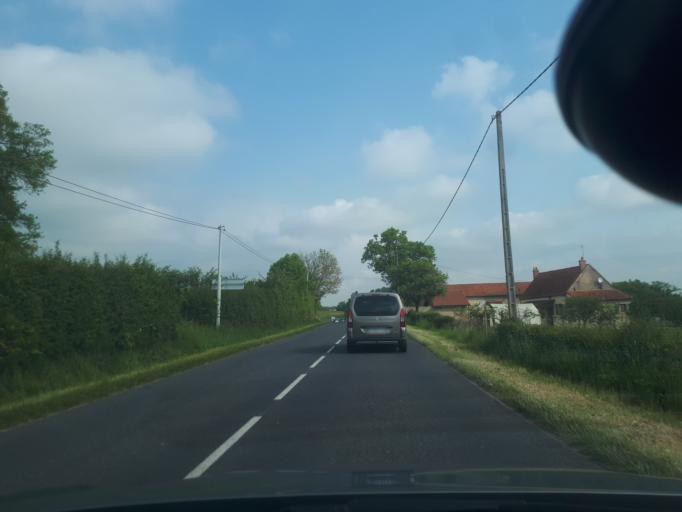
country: FR
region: Auvergne
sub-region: Departement de l'Allier
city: Lapalisse
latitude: 46.3314
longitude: 3.5820
